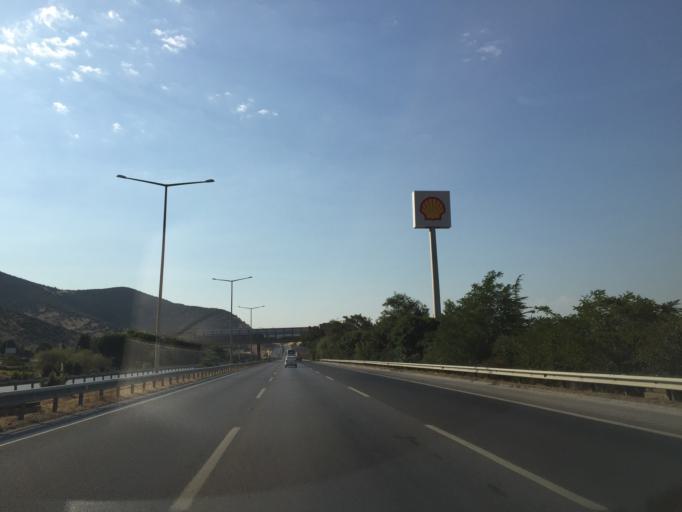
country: TR
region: Izmir
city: Belevi
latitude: 38.0688
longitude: 27.4127
